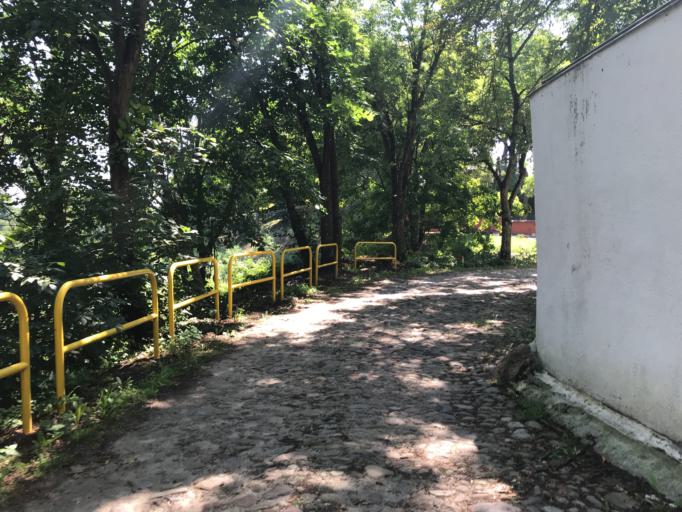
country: PL
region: Kujawsko-Pomorskie
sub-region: Powiat golubsko-dobrzynski
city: Zbojno
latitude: 53.0016
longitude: 19.2139
